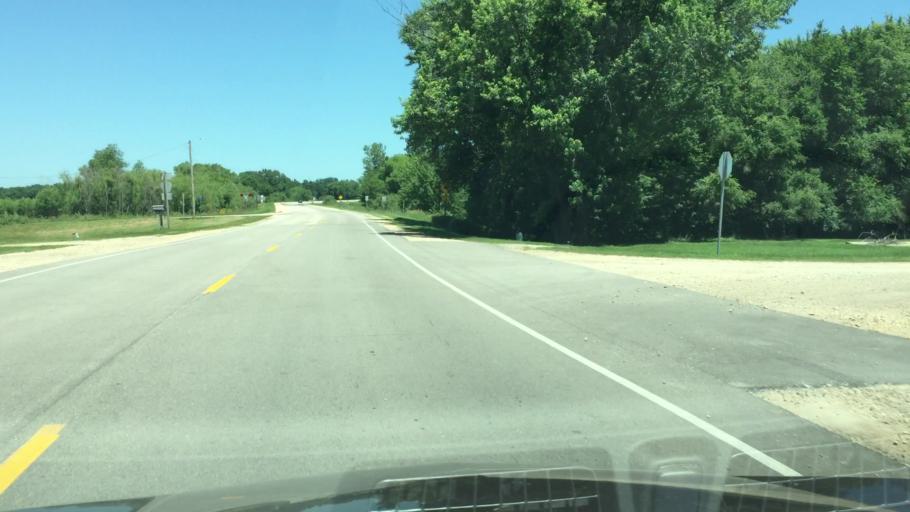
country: US
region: Iowa
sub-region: Cedar County
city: Mechanicsville
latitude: 42.0014
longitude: -91.1419
